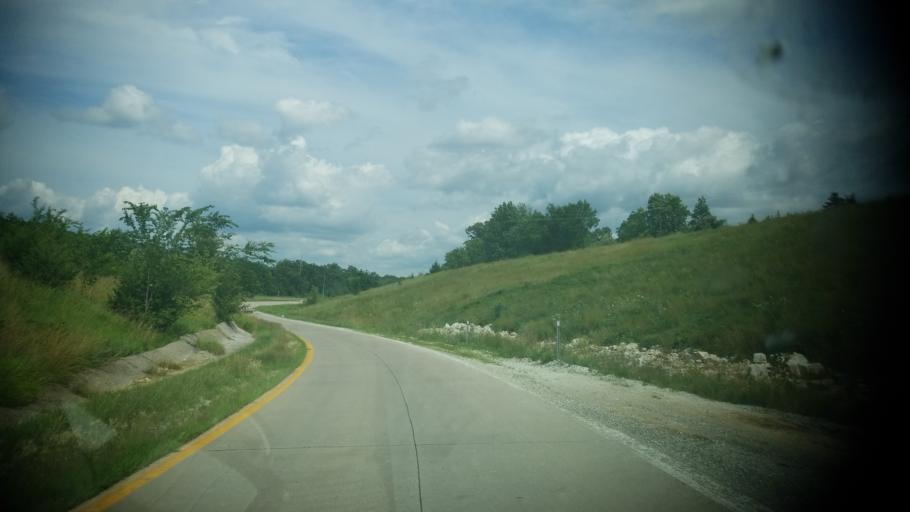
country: US
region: Missouri
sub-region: Pike County
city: Bowling Green
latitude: 39.3575
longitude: -91.2042
